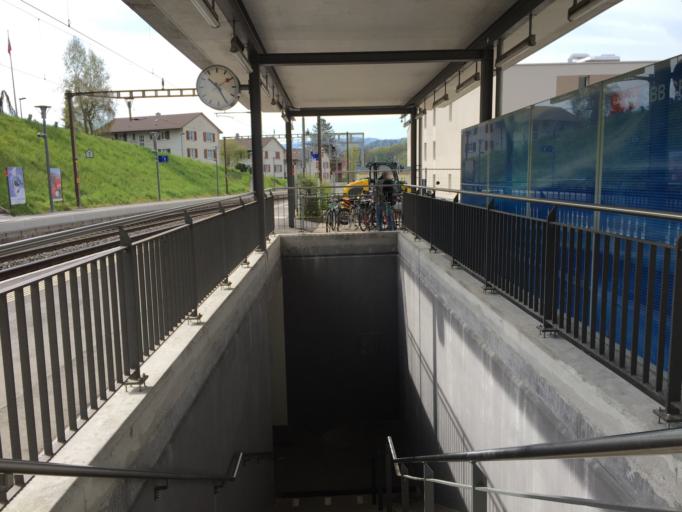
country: CH
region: Fribourg
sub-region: Sense District
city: Flamatt
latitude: 46.8937
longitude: 7.3518
